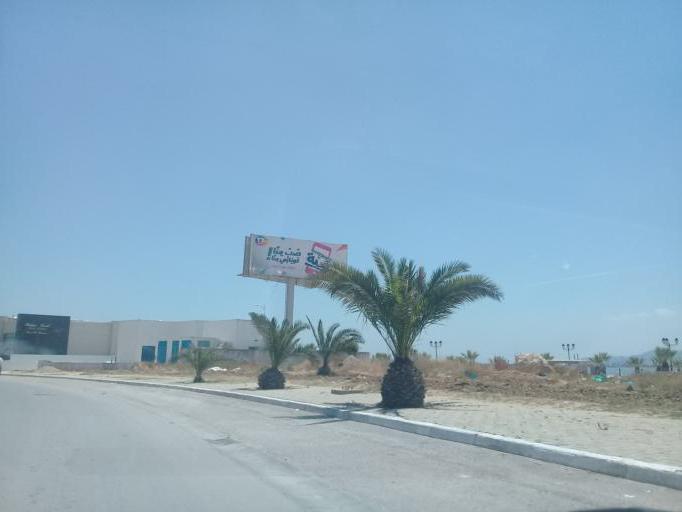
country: TN
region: Tunis
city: La Goulette
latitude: 36.8415
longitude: 10.2675
